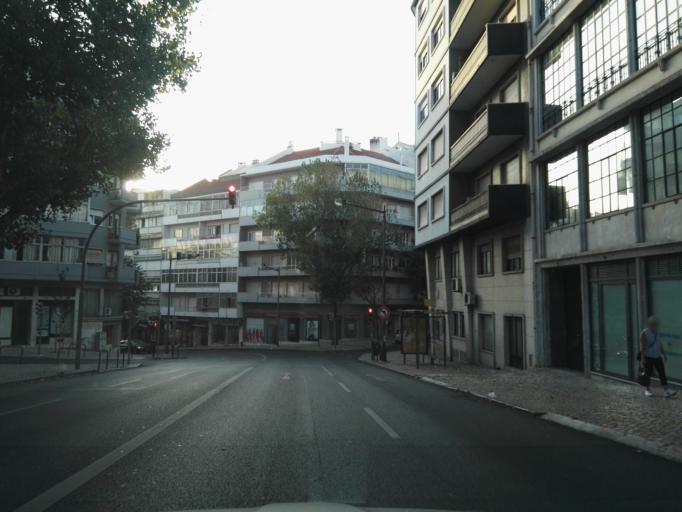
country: PT
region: Lisbon
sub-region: Lisbon
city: Lisbon
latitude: 38.7277
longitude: -9.1429
